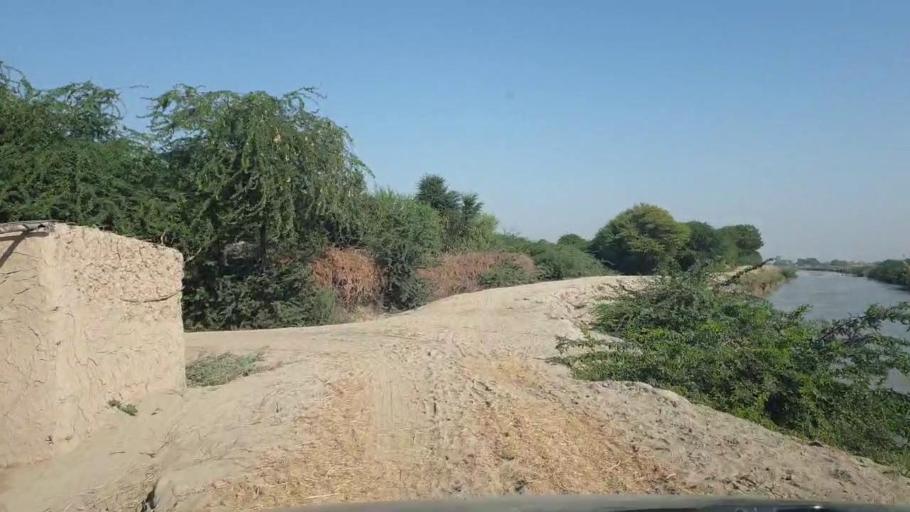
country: PK
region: Sindh
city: Badin
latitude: 24.7236
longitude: 68.8029
